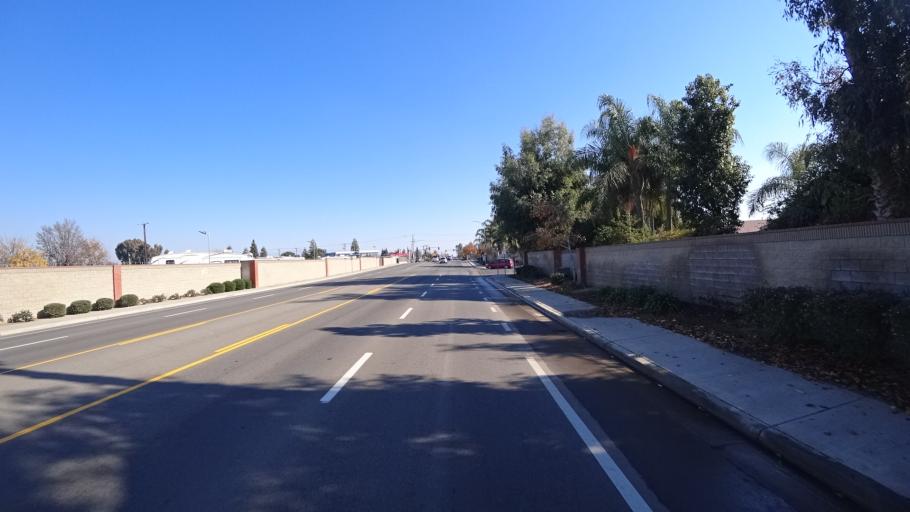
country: US
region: California
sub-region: Kern County
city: Greenfield
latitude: 35.3032
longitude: -119.0589
